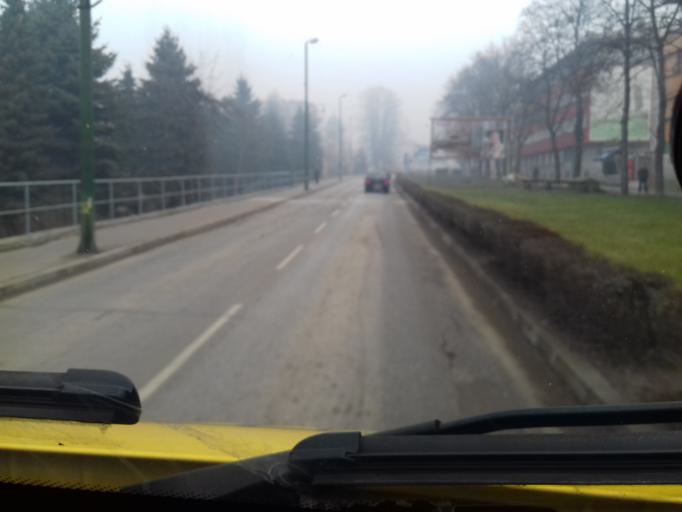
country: BA
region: Federation of Bosnia and Herzegovina
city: Kakanj
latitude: 44.1270
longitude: 18.1170
